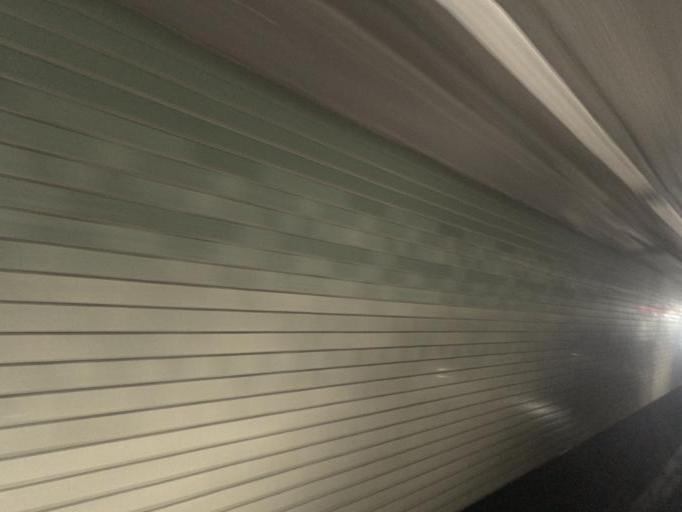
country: US
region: Hawaii
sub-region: Honolulu County
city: Kane'ohe
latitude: 21.3759
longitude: -157.8187
